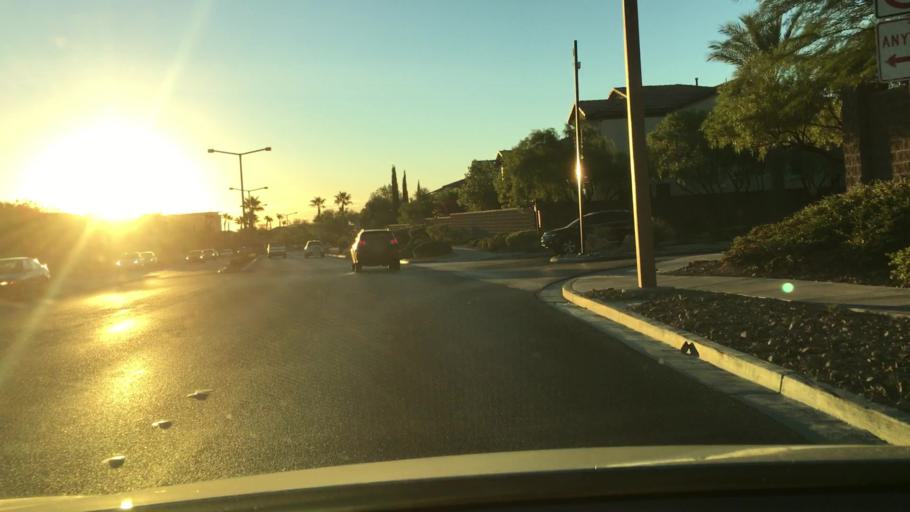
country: US
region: Nevada
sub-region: Clark County
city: Summerlin South
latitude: 36.1557
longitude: -115.3496
